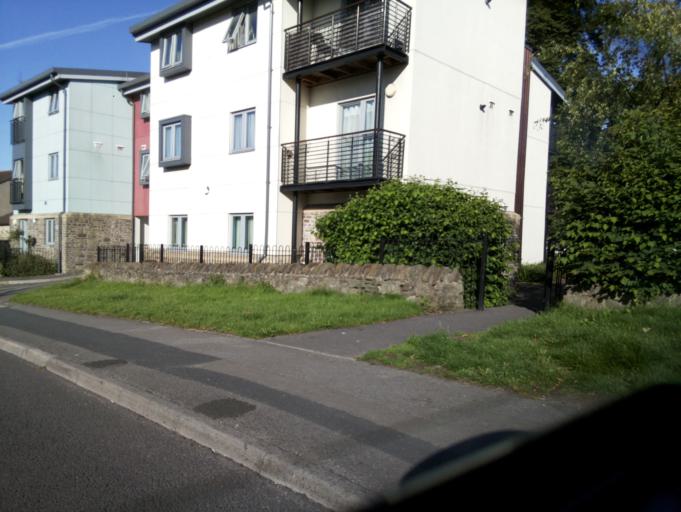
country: GB
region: England
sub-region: South Gloucestershire
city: Kingswood
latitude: 51.4484
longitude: -2.5212
